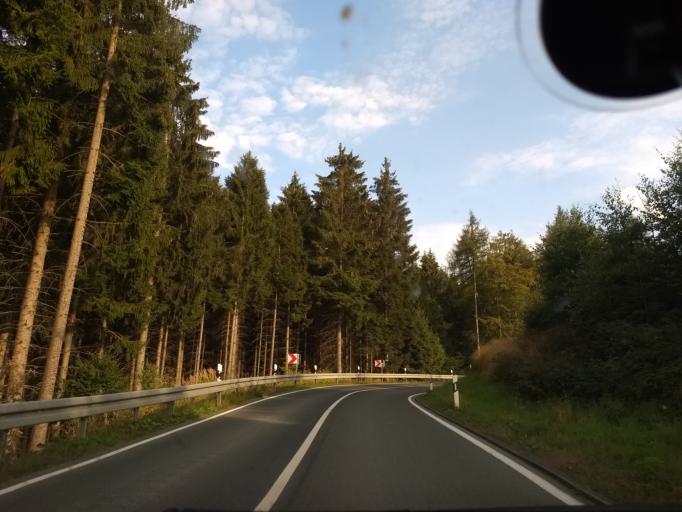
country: DE
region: North Rhine-Westphalia
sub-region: Regierungsbezirk Arnsberg
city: Arnsberg
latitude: 51.3552
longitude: 8.0664
